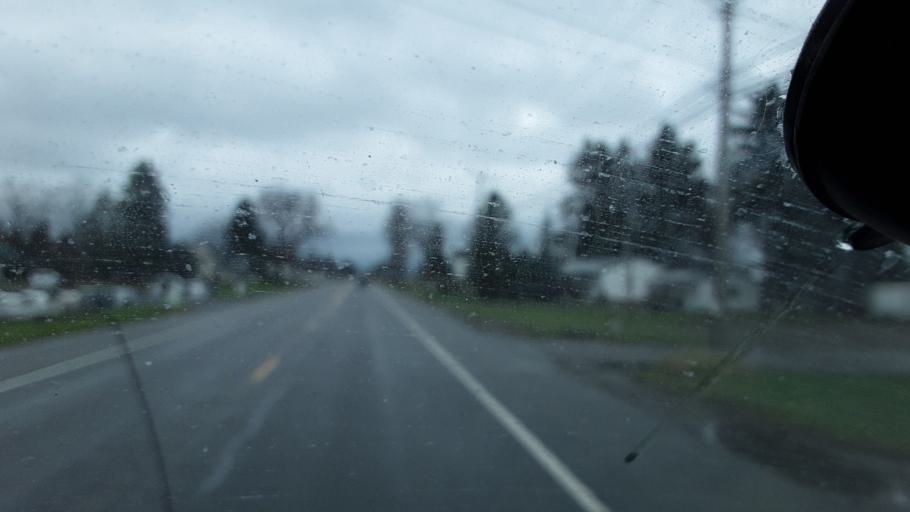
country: US
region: New York
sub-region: Cattaraugus County
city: Yorkshire
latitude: 42.5495
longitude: -78.4781
